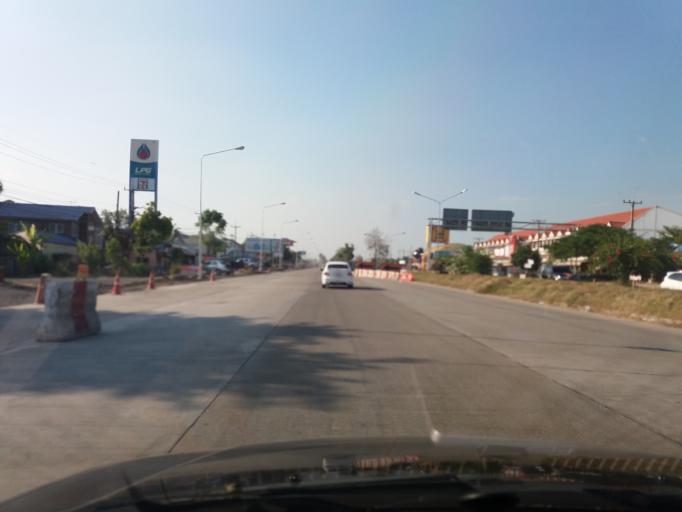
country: TH
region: Nakhon Sawan
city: Kao Liao
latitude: 15.7679
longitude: 99.9874
